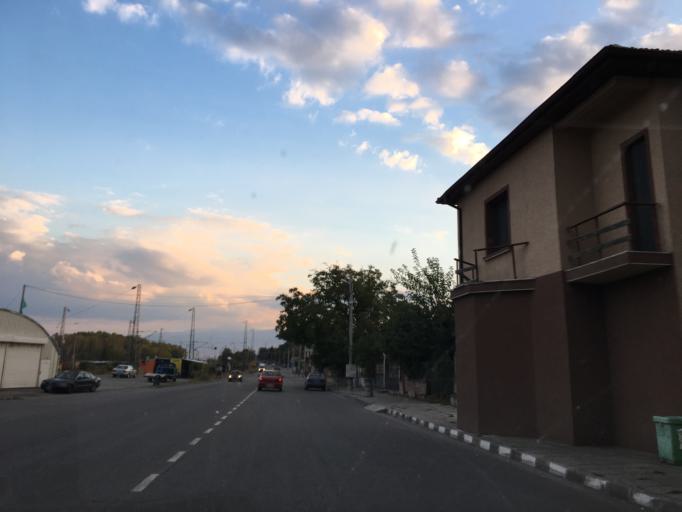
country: BG
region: Sofia-Capital
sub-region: Stolichna Obshtina
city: Sofia
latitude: 42.8167
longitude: 23.3527
